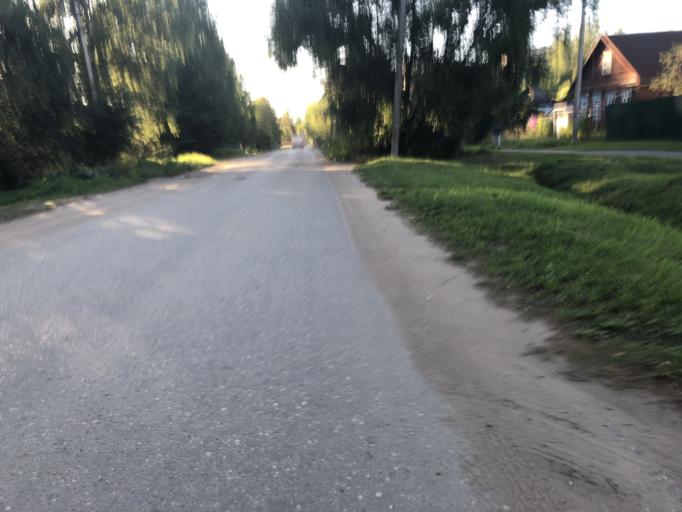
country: RU
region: Tverskaya
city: Rzhev
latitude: 56.2424
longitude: 34.3158
